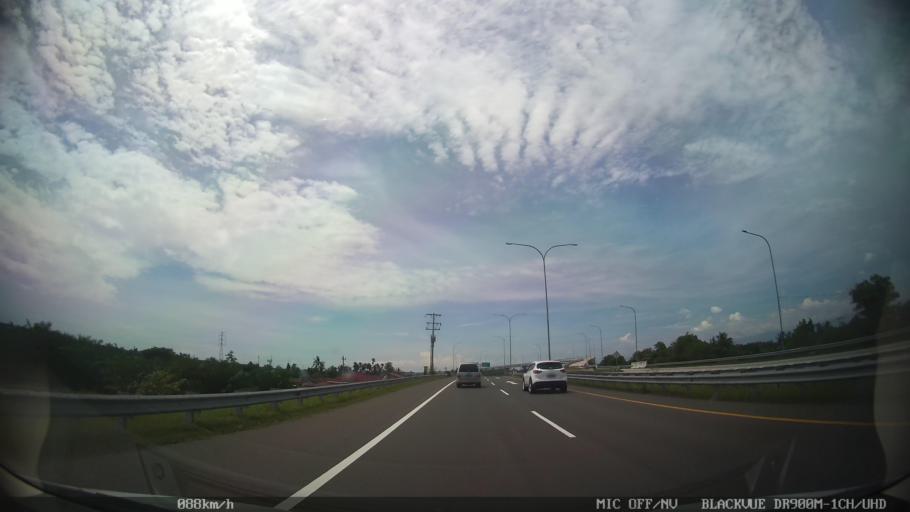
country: ID
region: North Sumatra
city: Percut
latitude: 3.5423
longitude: 98.8549
